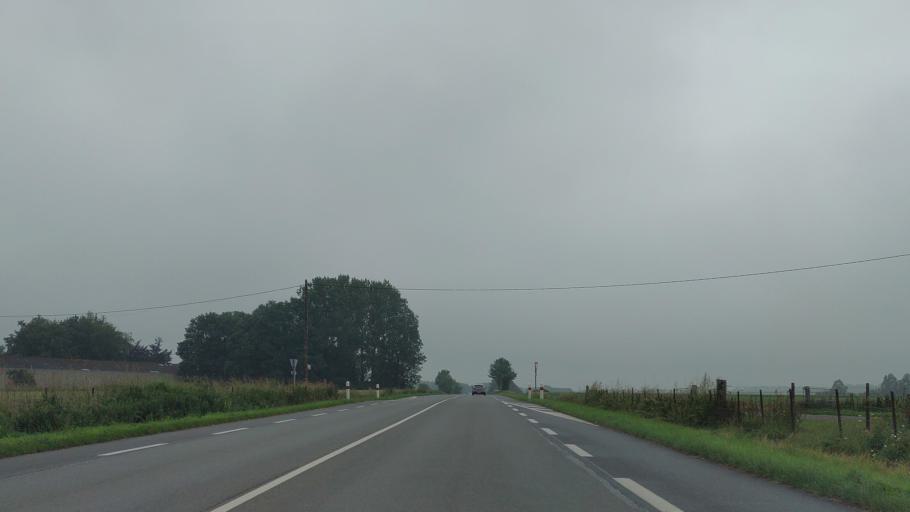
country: FR
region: Picardie
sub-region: Departement de la Somme
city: Fressenneville
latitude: 50.0743
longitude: 1.5776
